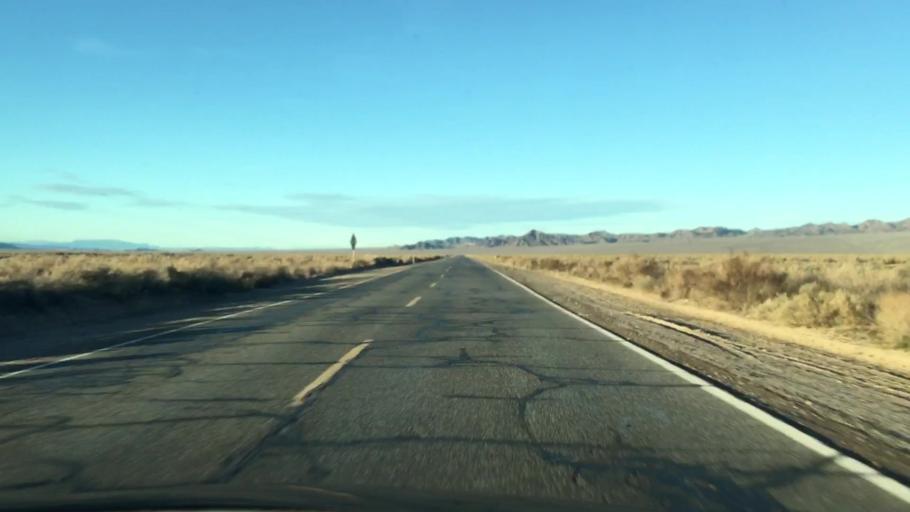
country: US
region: California
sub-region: San Bernardino County
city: Fort Irwin
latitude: 35.2992
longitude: -116.0830
